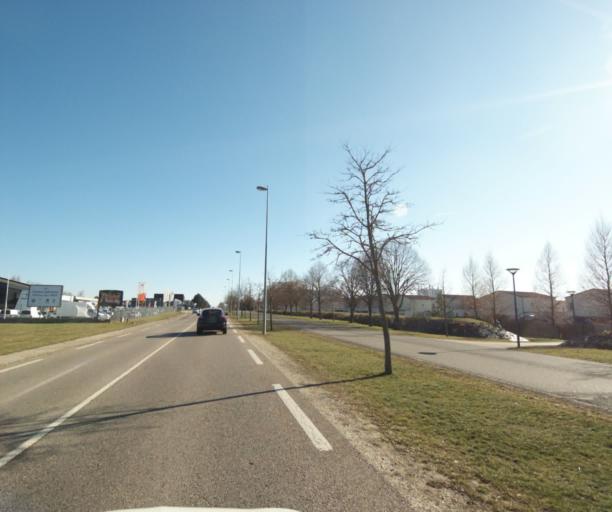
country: FR
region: Lorraine
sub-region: Departement de Meurthe-et-Moselle
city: Tomblaine
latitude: 48.6910
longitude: 6.2141
